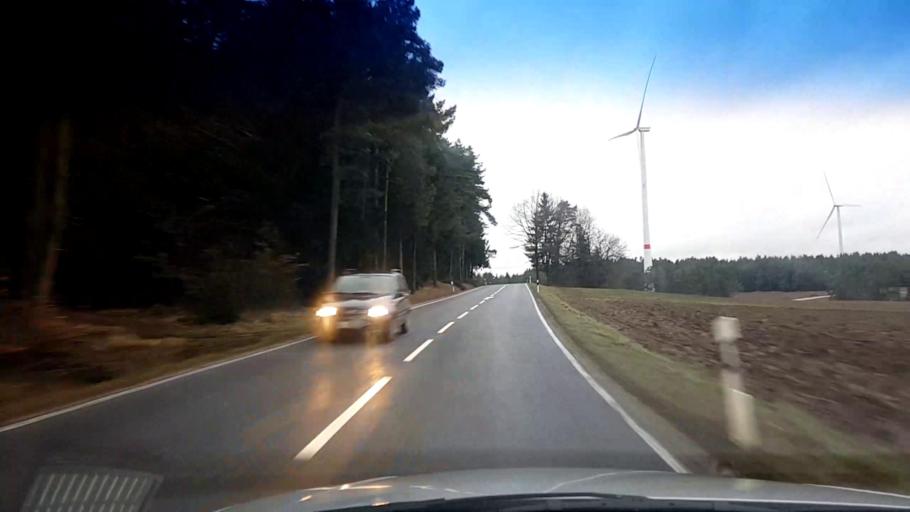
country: DE
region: Bavaria
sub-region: Upper Franconia
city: Wattendorf
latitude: 50.0130
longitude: 11.1308
